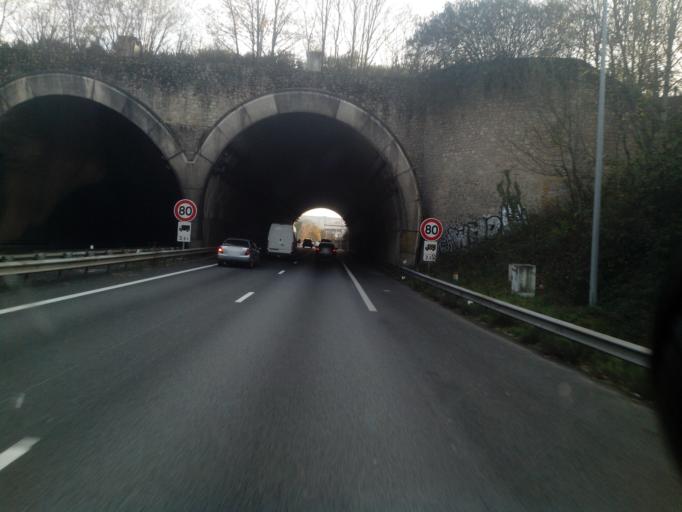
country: FR
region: Limousin
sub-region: Departement de la Haute-Vienne
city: Limoges
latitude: 45.8442
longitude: 1.2781
